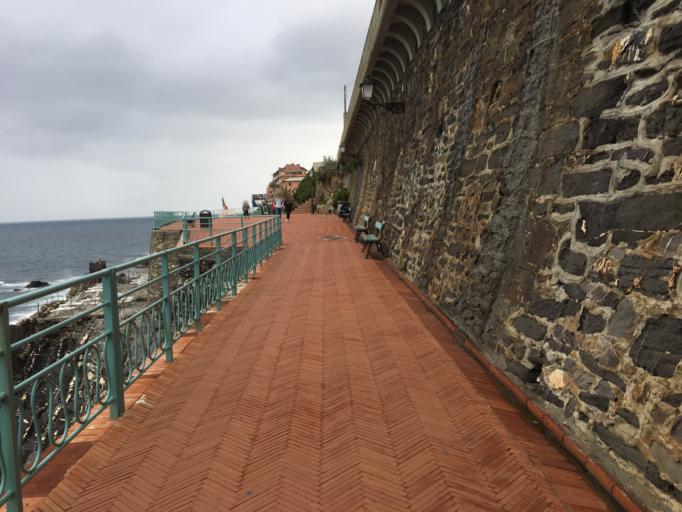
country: IT
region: Liguria
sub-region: Provincia di Genova
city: Bogliasco
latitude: 44.3813
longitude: 9.0389
